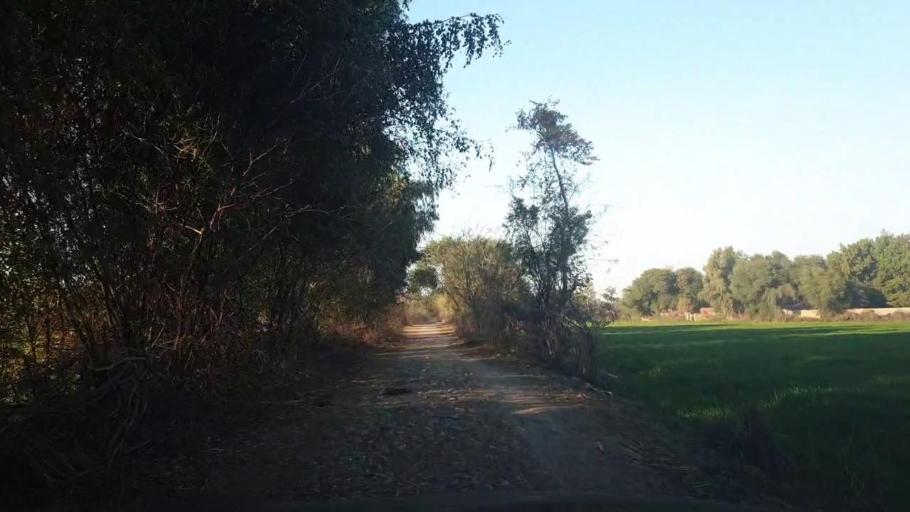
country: PK
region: Sindh
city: Mirpur Mathelo
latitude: 28.0070
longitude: 69.4612
